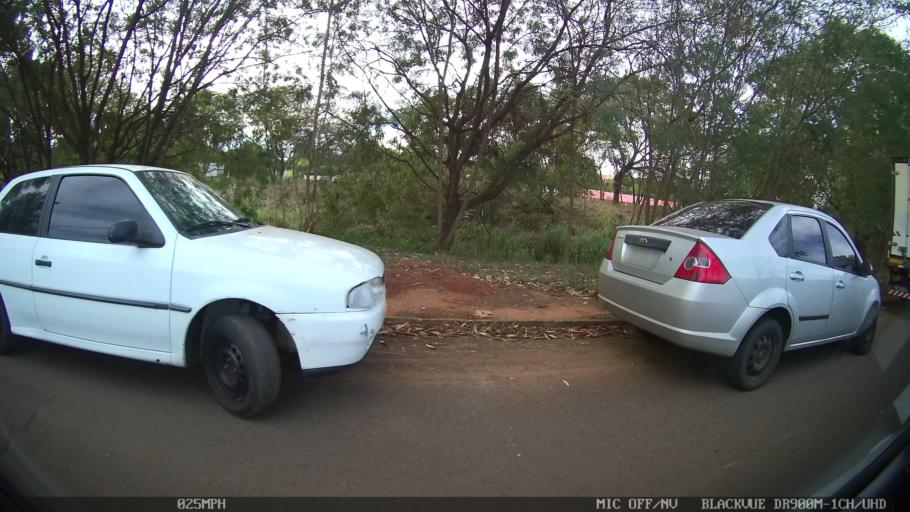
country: BR
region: Sao Paulo
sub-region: Catanduva
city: Catanduva
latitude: -21.1267
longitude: -48.9805
